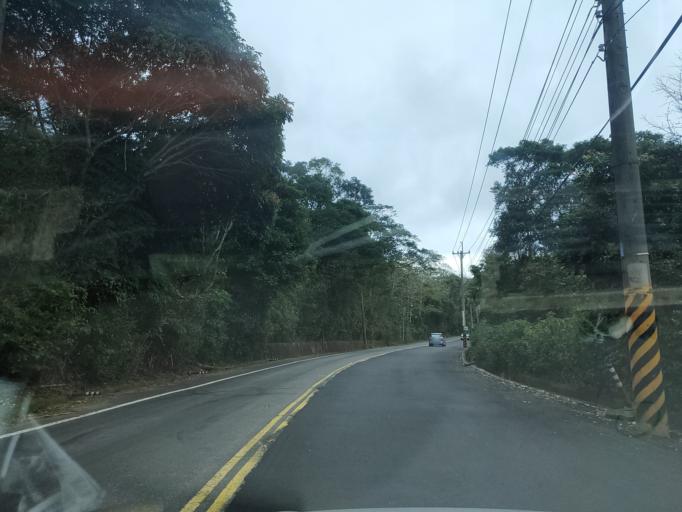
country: TW
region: Taiwan
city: Fengyuan
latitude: 24.3740
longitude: 120.7682
